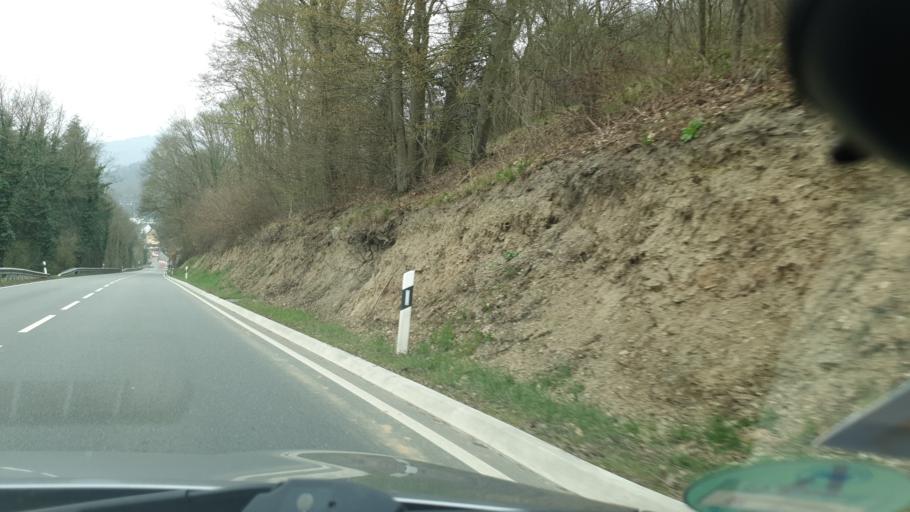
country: DE
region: Rheinland-Pfalz
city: Nassau
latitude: 50.3032
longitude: 7.8008
